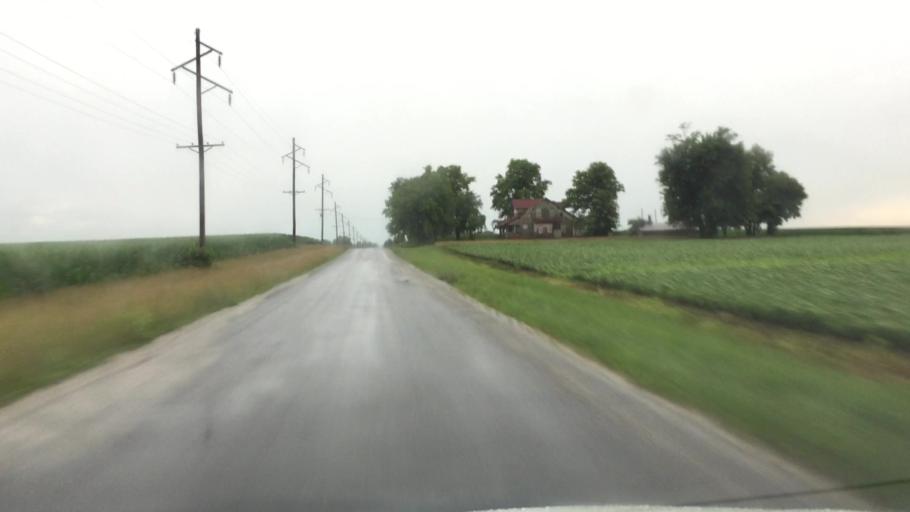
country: US
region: Illinois
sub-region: Hancock County
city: Hamilton
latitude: 40.4521
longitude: -91.2710
